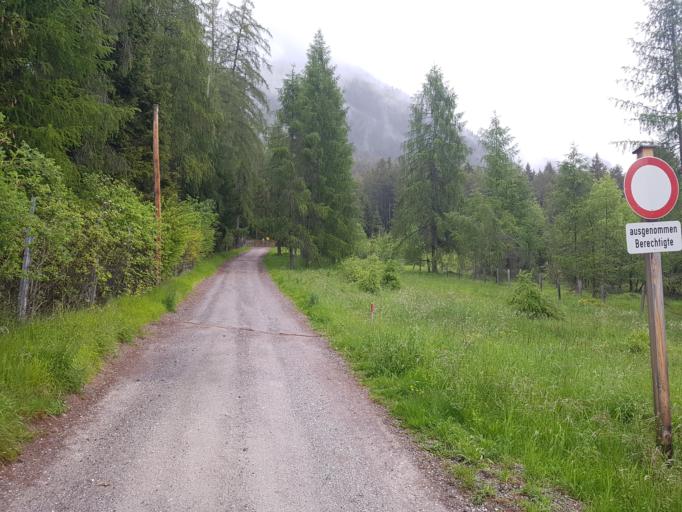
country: AT
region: Tyrol
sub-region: Politischer Bezirk Imst
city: Obsteig
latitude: 47.3032
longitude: 10.9229
